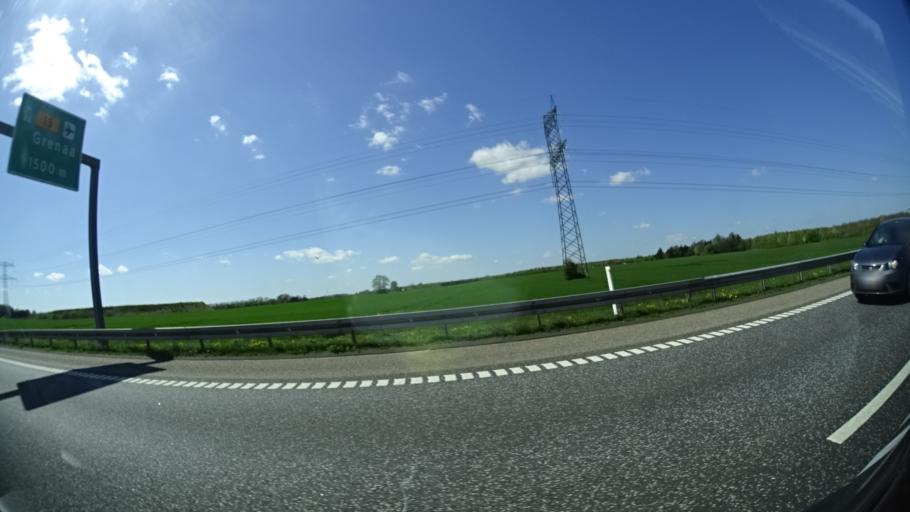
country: DK
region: Central Jutland
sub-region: Arhus Kommune
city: Trige
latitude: 56.2436
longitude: 10.1242
